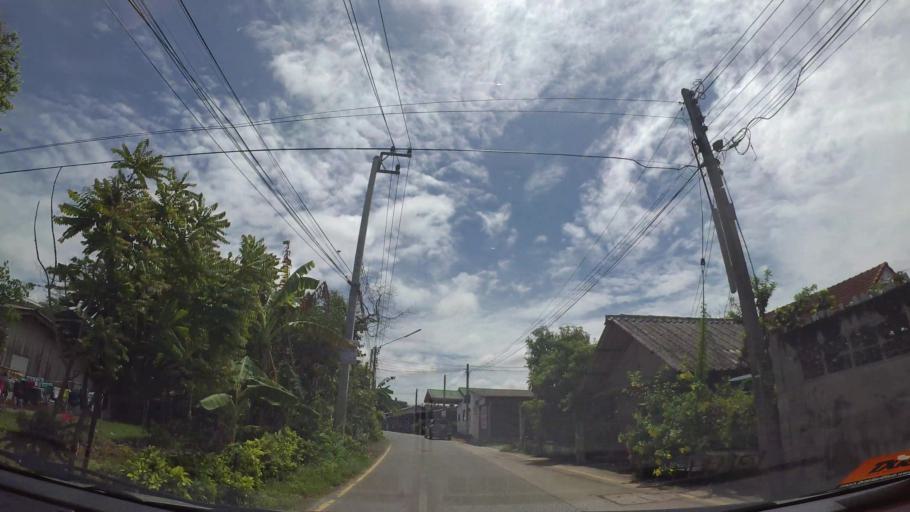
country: TH
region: Chon Buri
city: Sattahip
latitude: 12.7070
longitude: 100.8857
